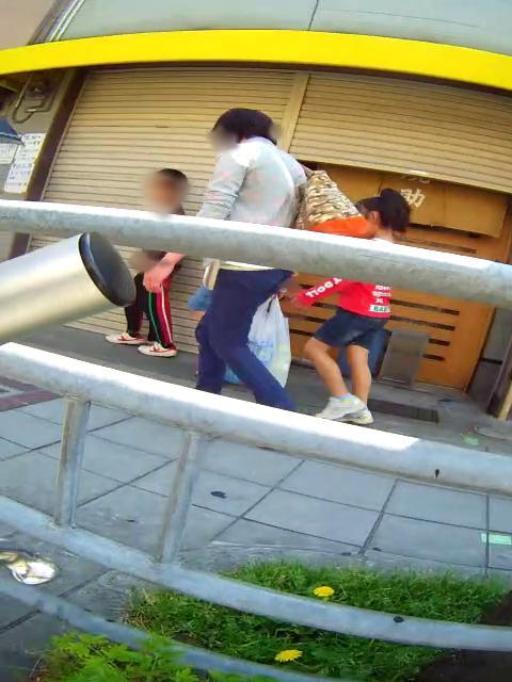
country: JP
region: Osaka
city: Yao
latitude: 34.6280
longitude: 135.5514
